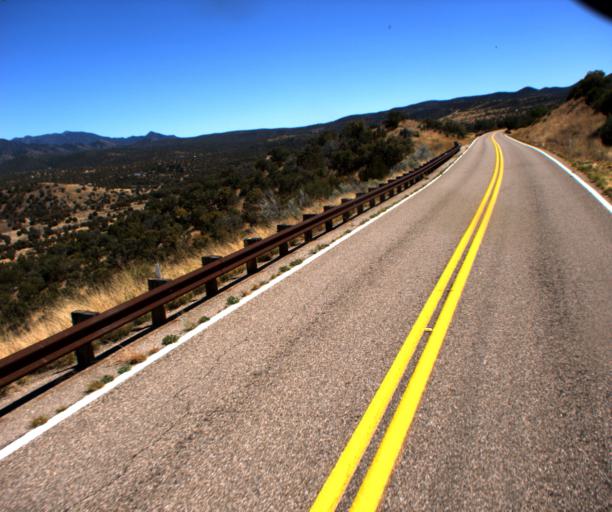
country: US
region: Arizona
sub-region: Cochise County
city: Sierra Vista
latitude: 31.5116
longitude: -110.4967
